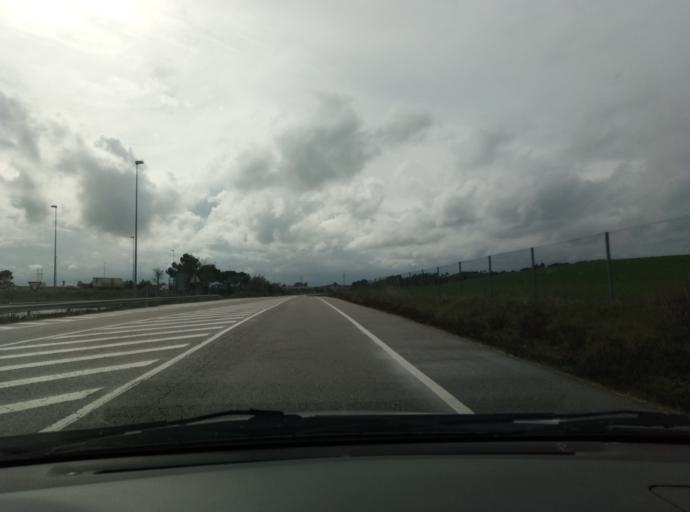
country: ES
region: Catalonia
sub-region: Provincia de Lleida
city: Sant Guim de Freixenet
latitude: 41.6219
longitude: 1.3908
